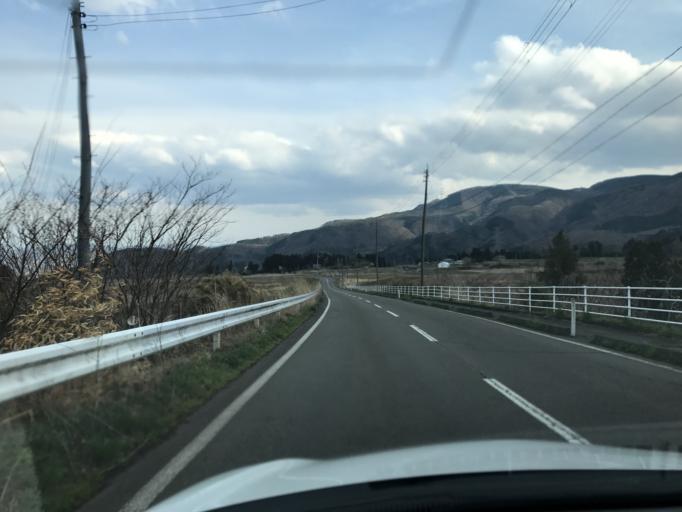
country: JP
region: Miyagi
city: Shiroishi
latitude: 38.0154
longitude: 140.5830
